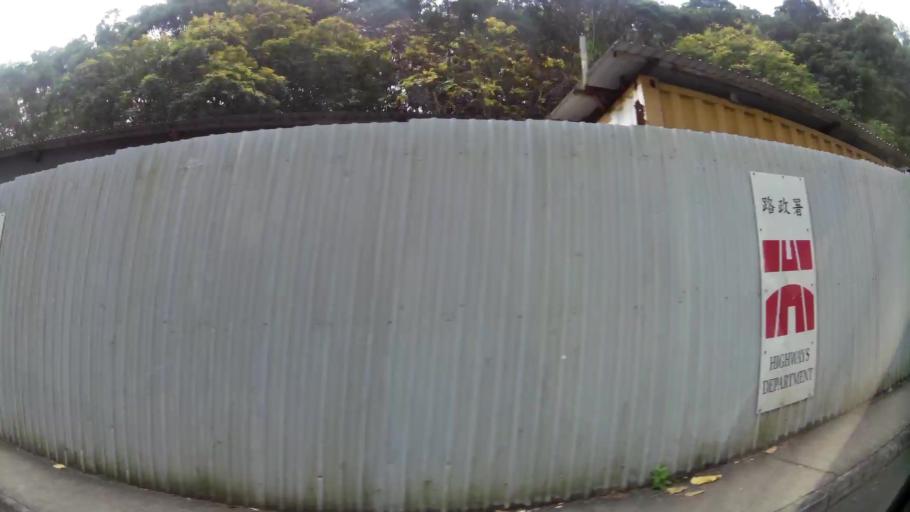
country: HK
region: Wanchai
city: Wan Chai
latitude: 22.2612
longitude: 114.2332
